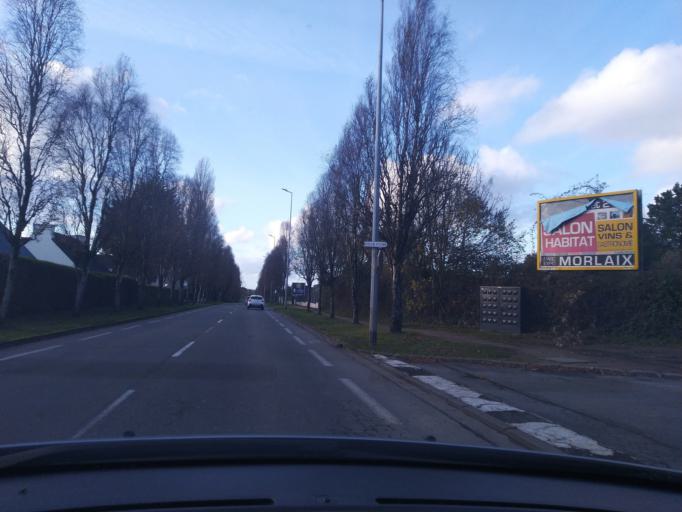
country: FR
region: Brittany
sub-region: Departement du Finistere
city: Morlaix
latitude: 48.5826
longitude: -3.8128
